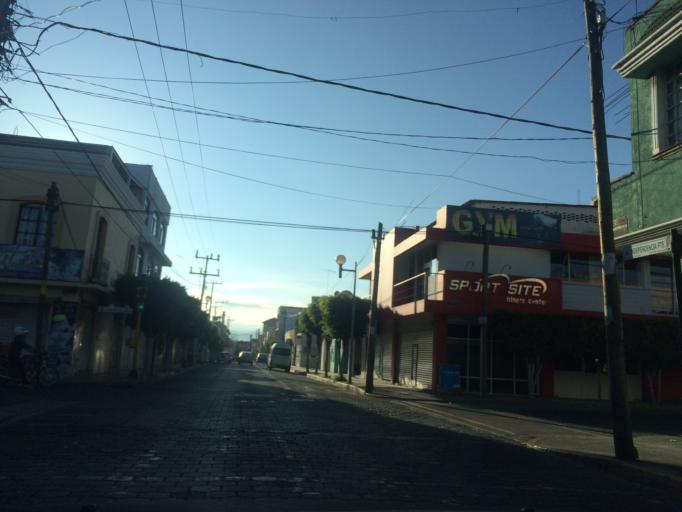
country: MX
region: Puebla
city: Tehuacan
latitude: 18.4631
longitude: -97.3984
